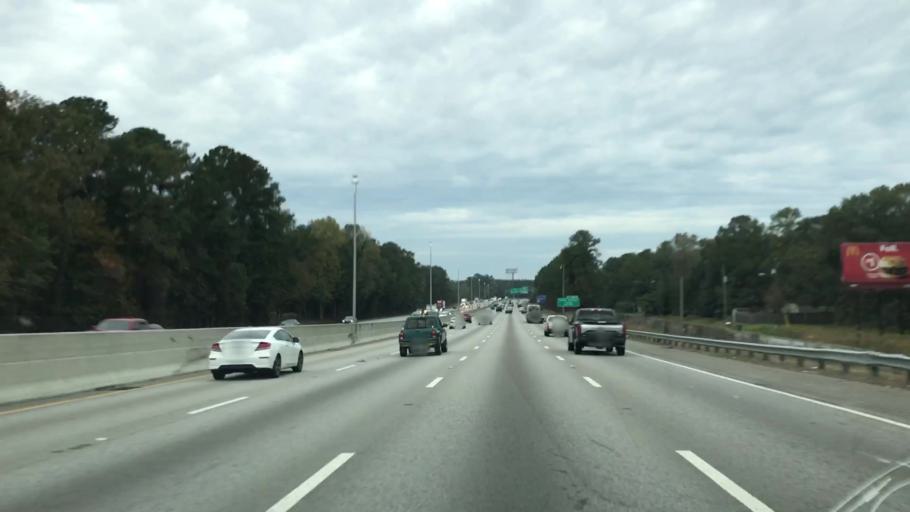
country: US
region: South Carolina
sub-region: Berkeley County
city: Hanahan
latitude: 32.9220
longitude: -80.0382
